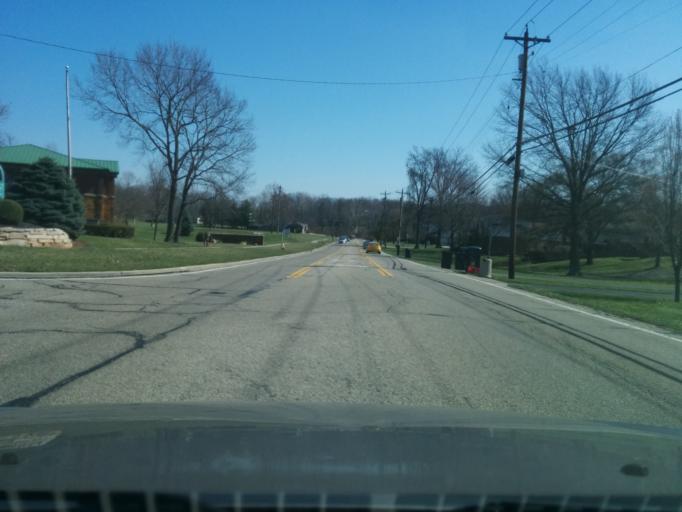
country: US
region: Ohio
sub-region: Hamilton County
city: Dry Ridge
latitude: 39.2449
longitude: -84.6109
